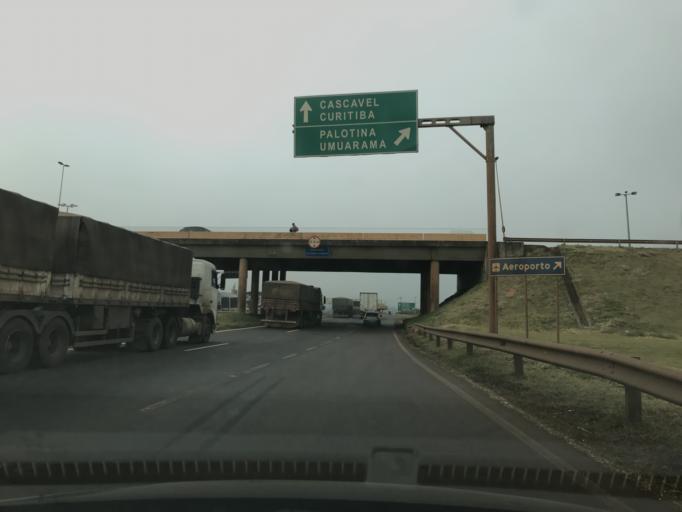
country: BR
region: Parana
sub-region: Toledo
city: Toledo
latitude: -24.7176
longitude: -53.7118
